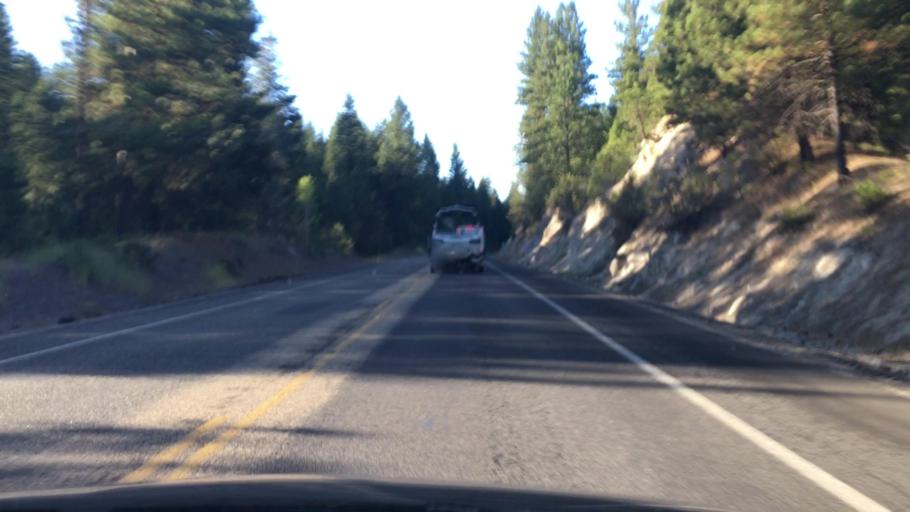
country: US
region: Idaho
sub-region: Valley County
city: Cascade
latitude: 44.5636
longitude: -116.0299
